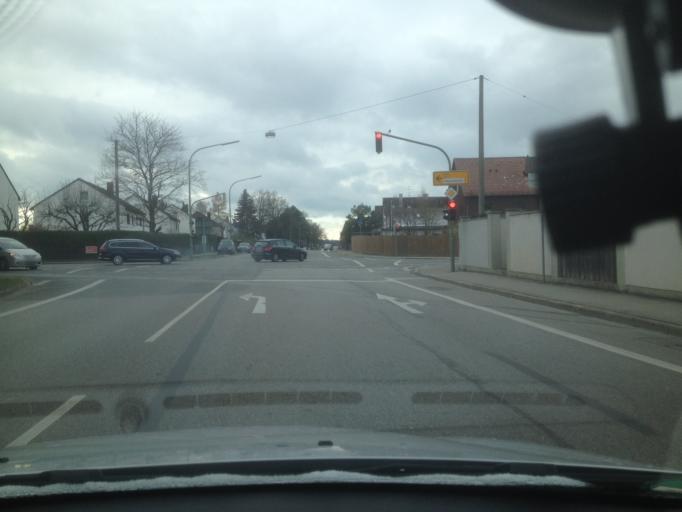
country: DE
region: Bavaria
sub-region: Swabia
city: Stadtbergen
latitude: 48.3329
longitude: 10.8711
